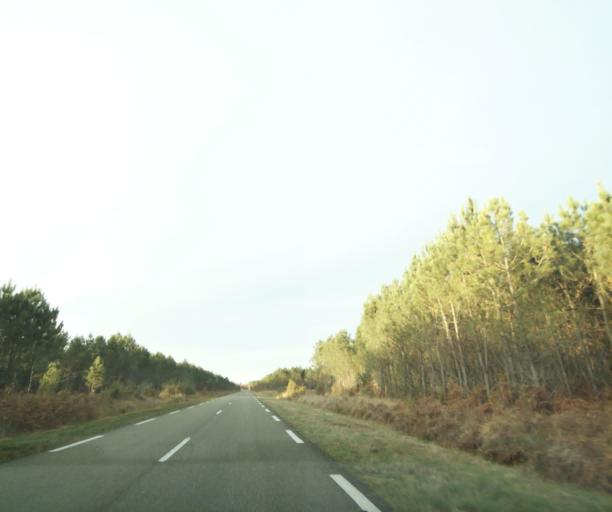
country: FR
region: Aquitaine
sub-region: Departement des Landes
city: Roquefort
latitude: 44.1832
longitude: -0.1480
